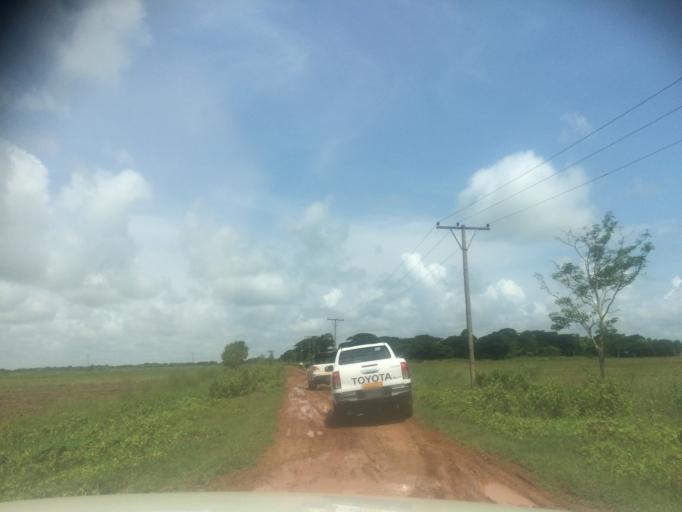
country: MM
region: Bago
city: Tharyarwady
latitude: 17.3175
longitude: 95.8996
